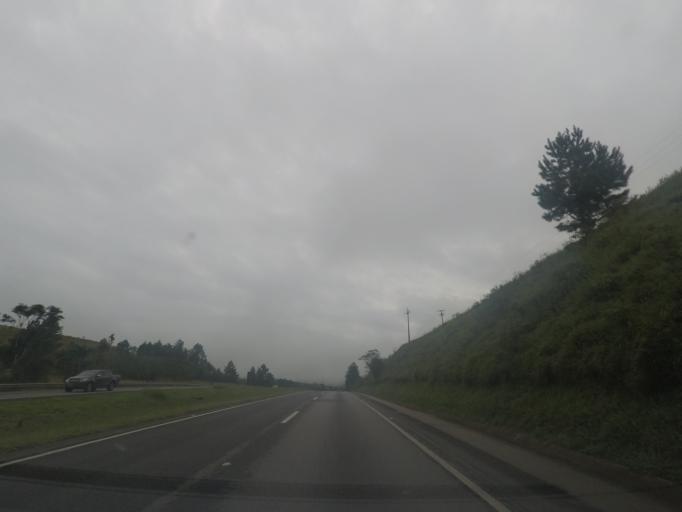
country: BR
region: Parana
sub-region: Antonina
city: Antonina
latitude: -25.0802
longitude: -48.5975
